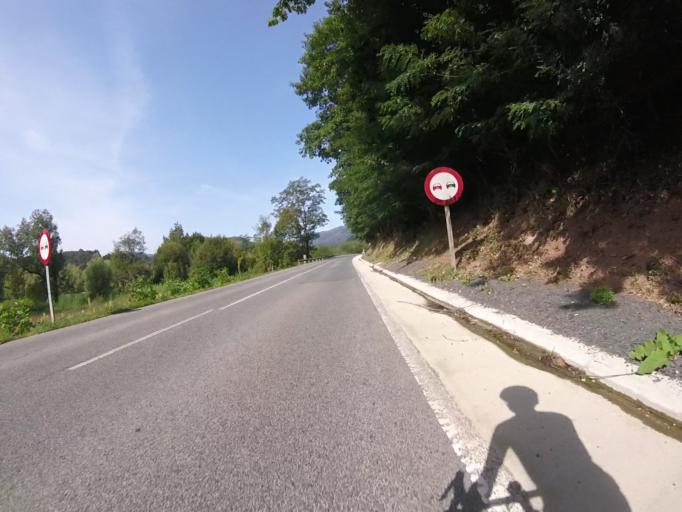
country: ES
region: Navarre
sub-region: Provincia de Navarra
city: Doneztebe
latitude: 43.1320
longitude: -1.6571
